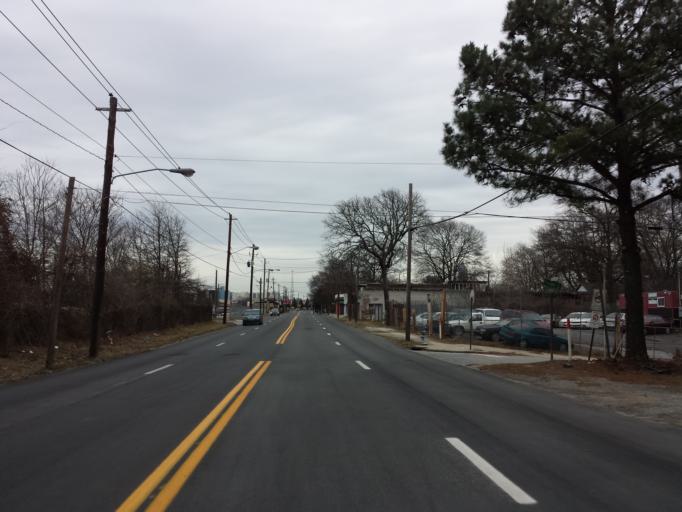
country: US
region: Georgia
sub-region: Fulton County
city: Atlanta
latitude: 33.7857
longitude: -84.4253
